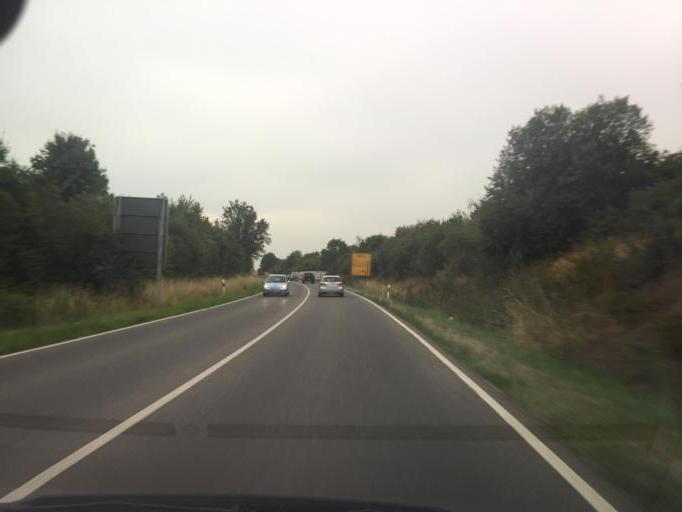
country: DE
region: North Rhine-Westphalia
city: Wegberg
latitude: 51.1557
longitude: 6.3514
